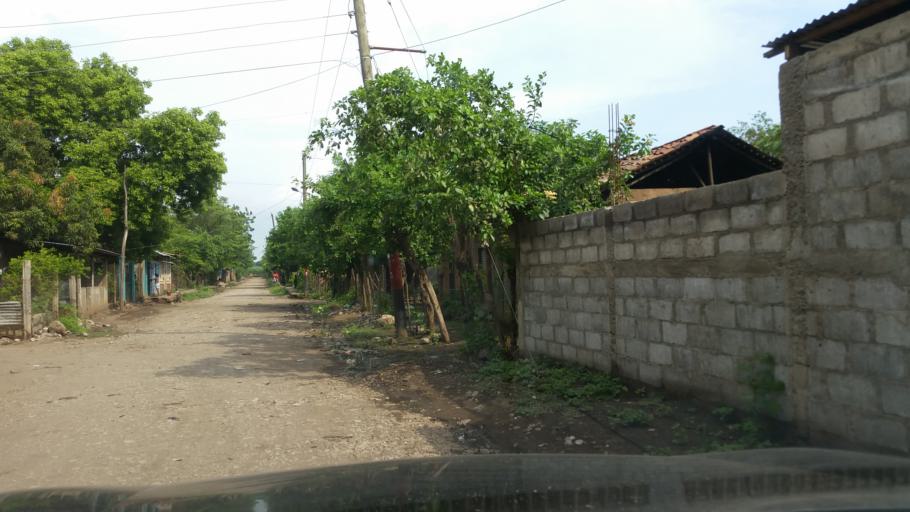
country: NI
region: Chinandega
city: Puerto Morazan
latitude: 12.7655
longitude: -87.1299
